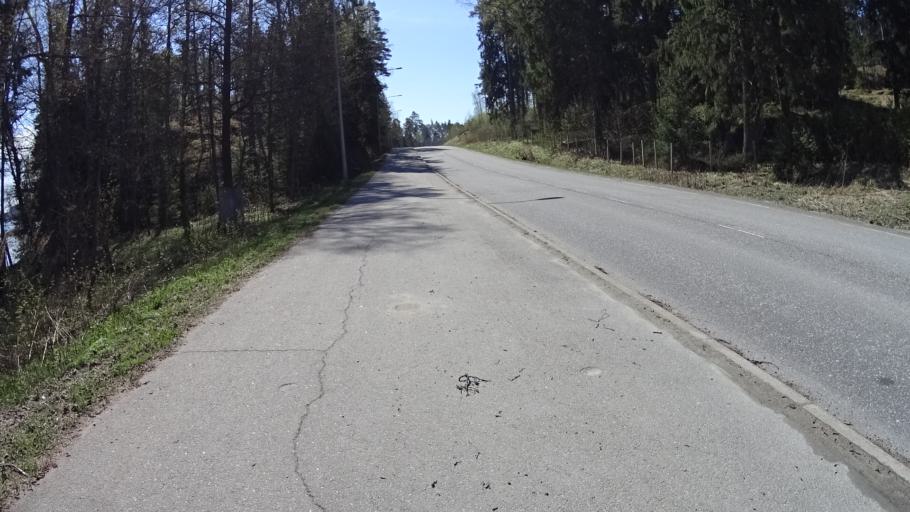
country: FI
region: Uusimaa
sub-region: Helsinki
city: Espoo
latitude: 60.2499
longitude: 24.6552
